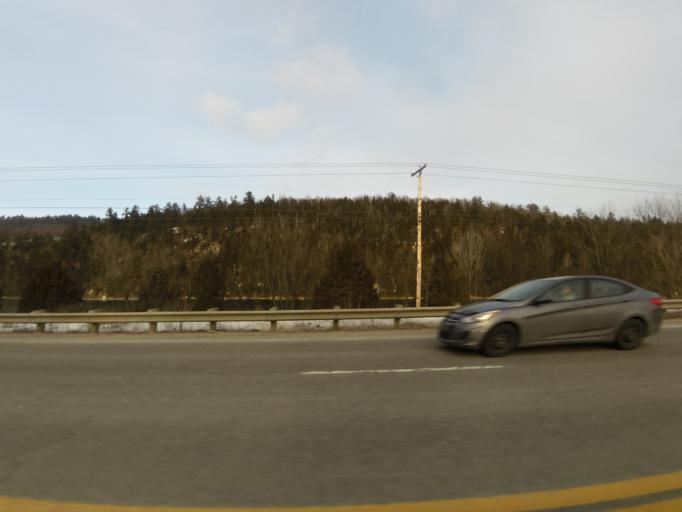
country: CA
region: Quebec
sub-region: Outaouais
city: Wakefield
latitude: 45.7532
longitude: -75.9161
